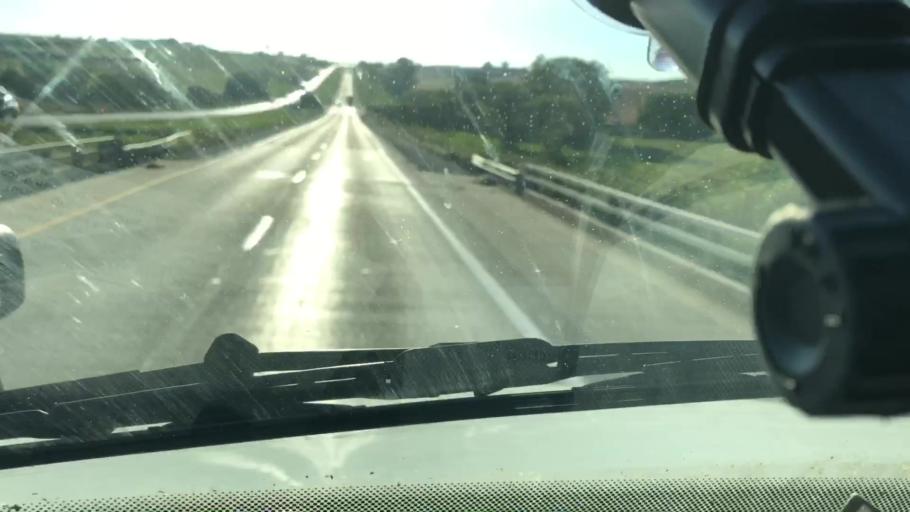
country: US
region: Iowa
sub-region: Pottawattamie County
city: Avoca
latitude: 41.4998
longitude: -95.5297
